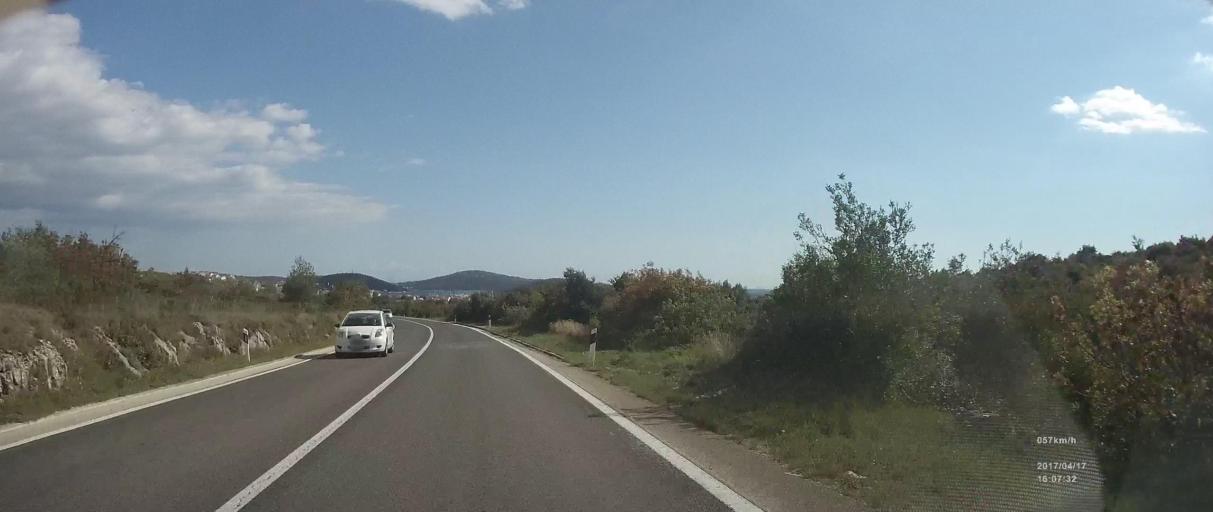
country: HR
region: Sibensko-Kniniska
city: Rogoznica
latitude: 43.5488
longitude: 15.9605
